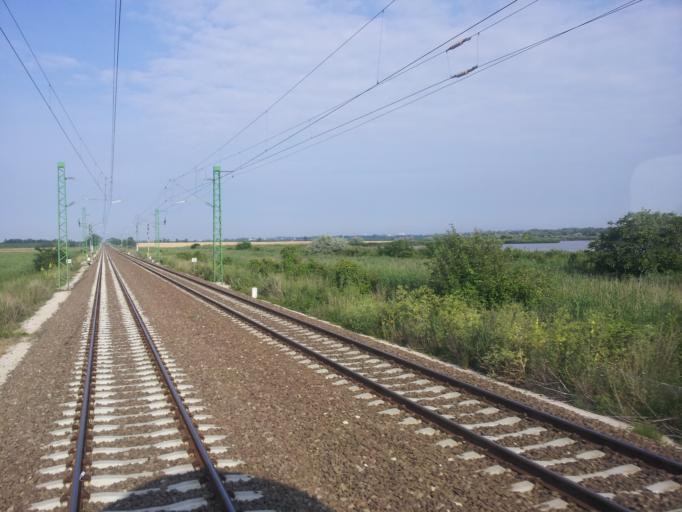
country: HU
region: Fejer
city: Pakozd
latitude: 47.1758
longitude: 18.5368
